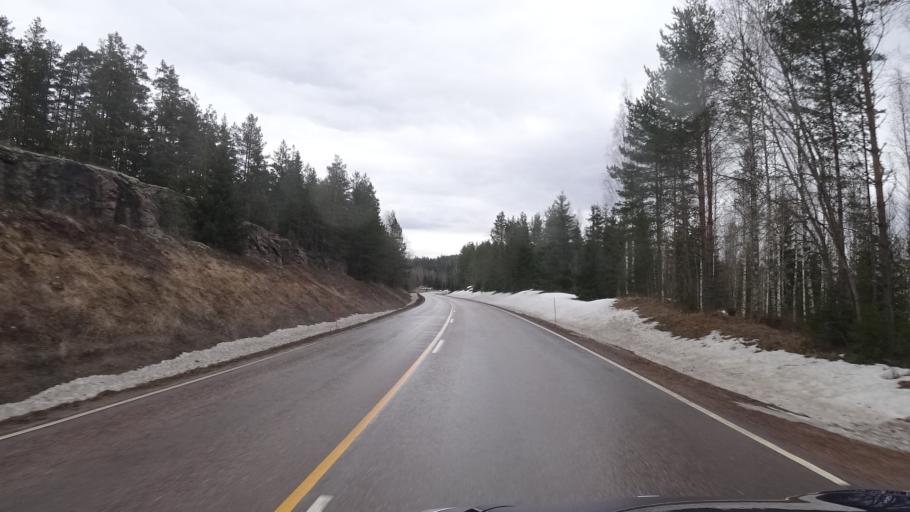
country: FI
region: Uusimaa
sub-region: Loviisa
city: Lapinjaervi
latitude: 60.7347
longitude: 26.1909
